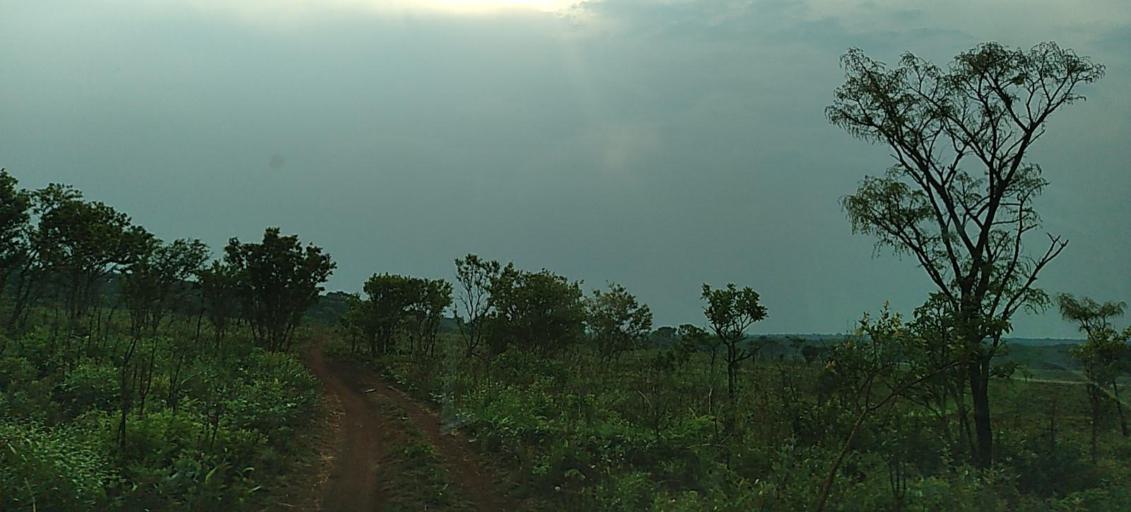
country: ZM
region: North-Western
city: Solwezi
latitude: -12.0431
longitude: 26.0279
